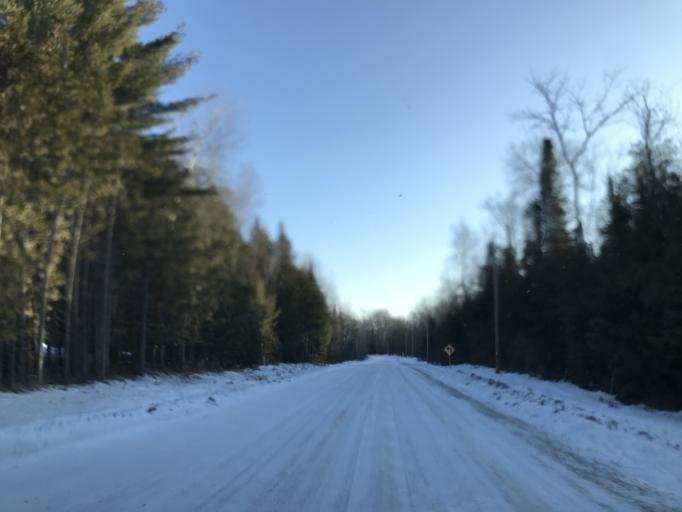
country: US
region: Michigan
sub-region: Menominee County
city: Menominee
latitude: 45.2904
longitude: -87.6991
